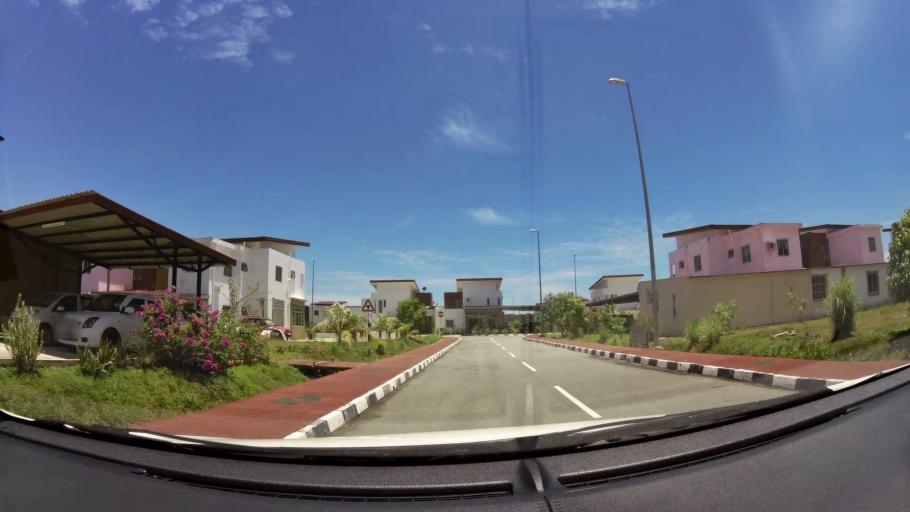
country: BN
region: Brunei and Muara
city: Bandar Seri Begawan
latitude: 5.0150
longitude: 115.0155
